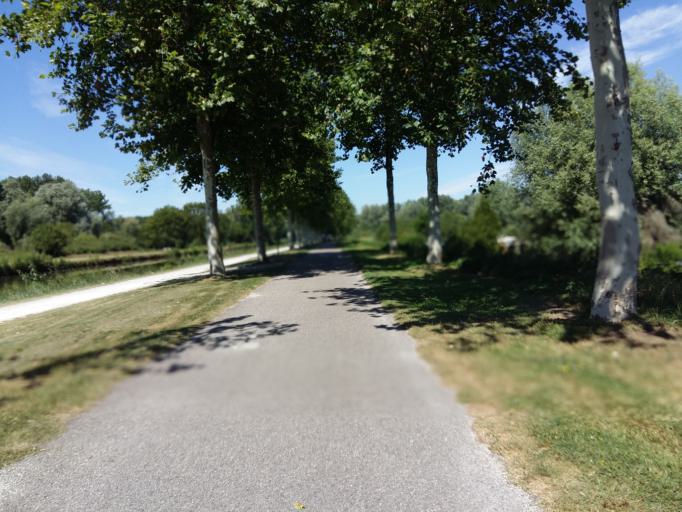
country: FR
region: Picardie
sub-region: Departement de la Somme
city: Amiens
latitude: 49.9139
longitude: 2.2738
